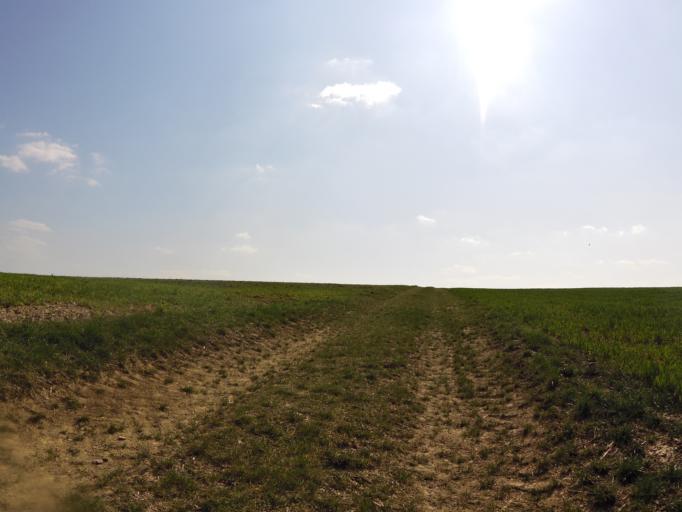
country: DE
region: Bavaria
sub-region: Regierungsbezirk Unterfranken
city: Dettelbach
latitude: 49.8175
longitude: 10.1444
